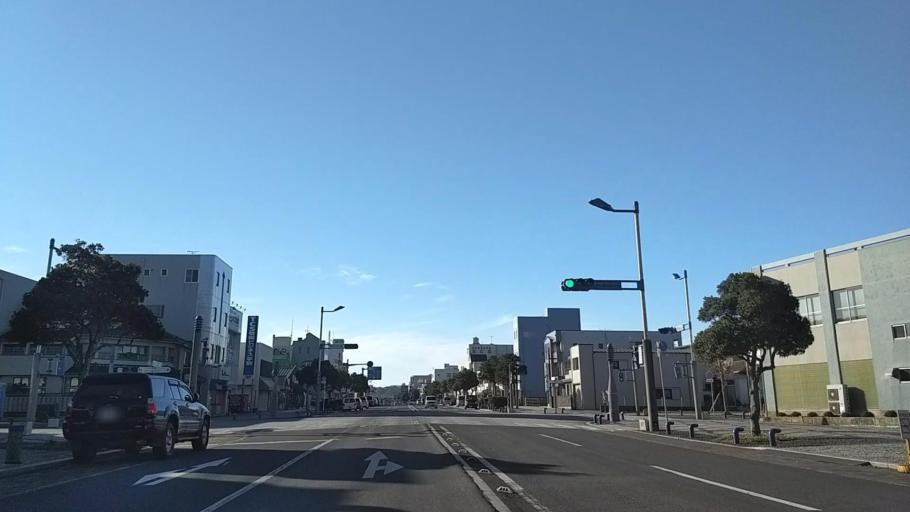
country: JP
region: Chiba
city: Hasaki
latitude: 35.7345
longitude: 140.8286
